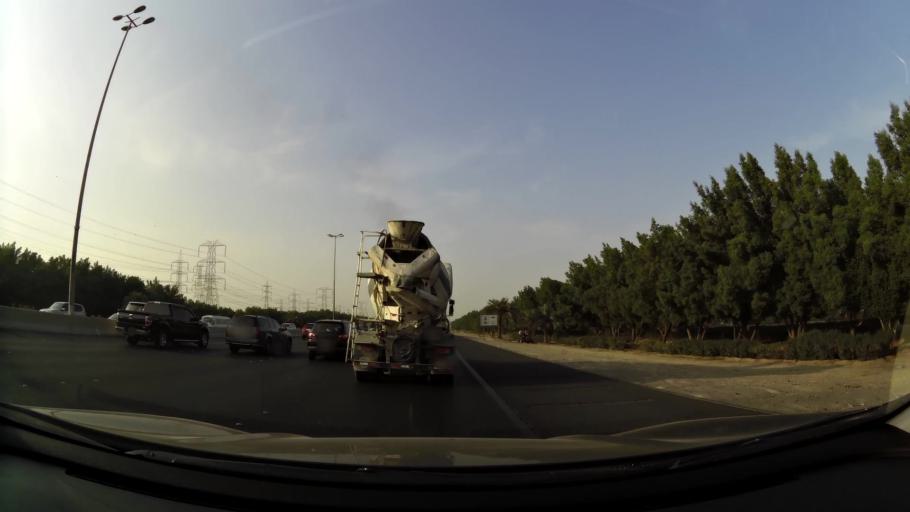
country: KW
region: Mubarak al Kabir
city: Sabah as Salim
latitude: 29.2247
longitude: 48.0545
